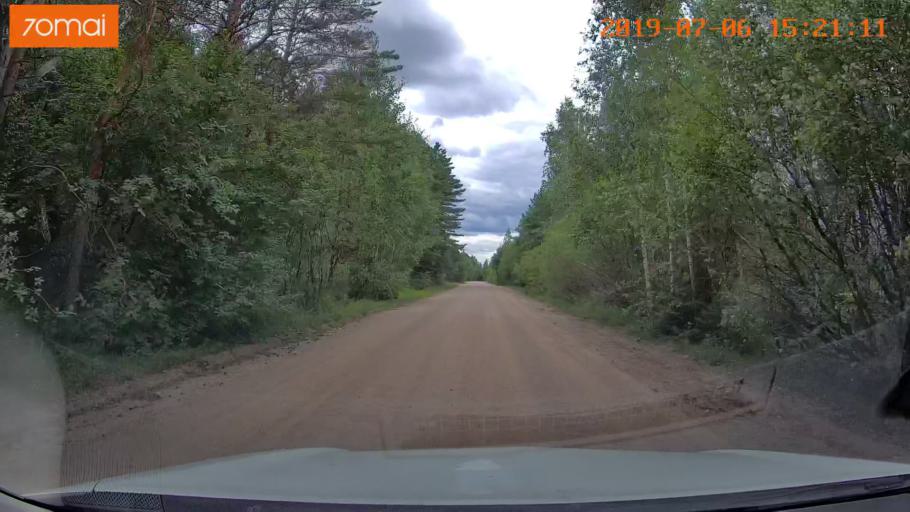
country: BY
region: Minsk
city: Valozhyn
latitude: 54.0097
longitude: 26.6195
